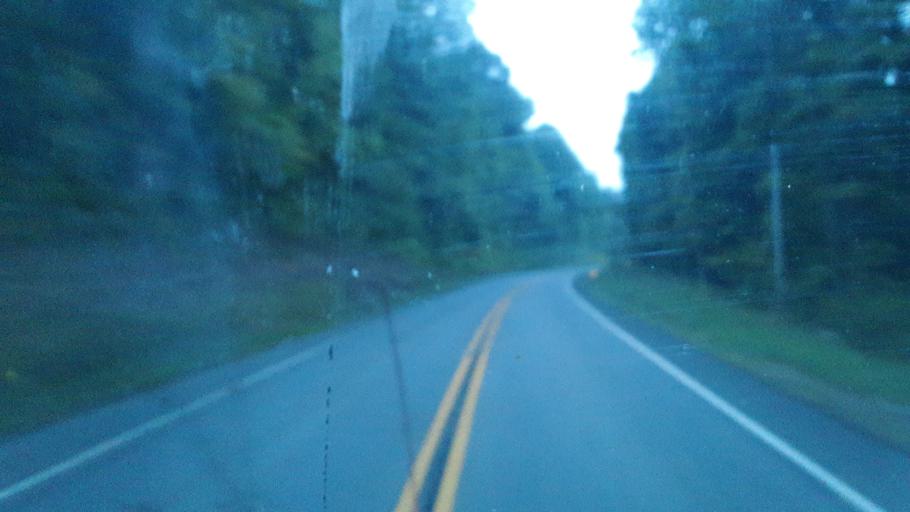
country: US
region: Pennsylvania
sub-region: Clarion County
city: Clarion
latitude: 41.0573
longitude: -79.3210
